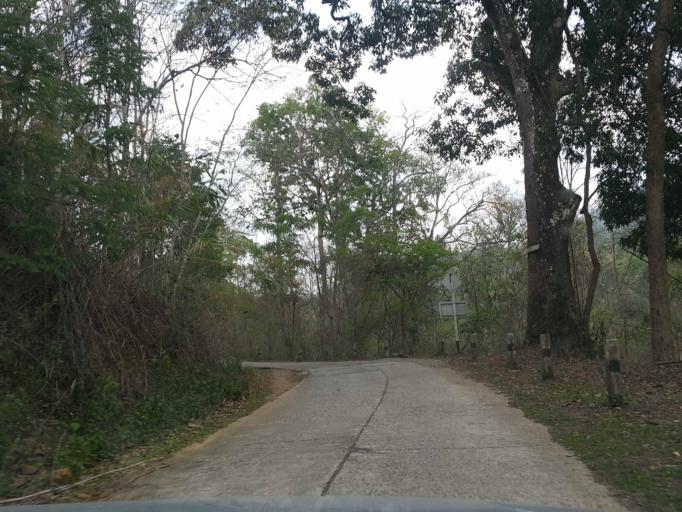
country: TH
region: Chiang Mai
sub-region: Amphoe Chiang Dao
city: Chiang Dao
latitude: 19.3807
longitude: 98.7694
